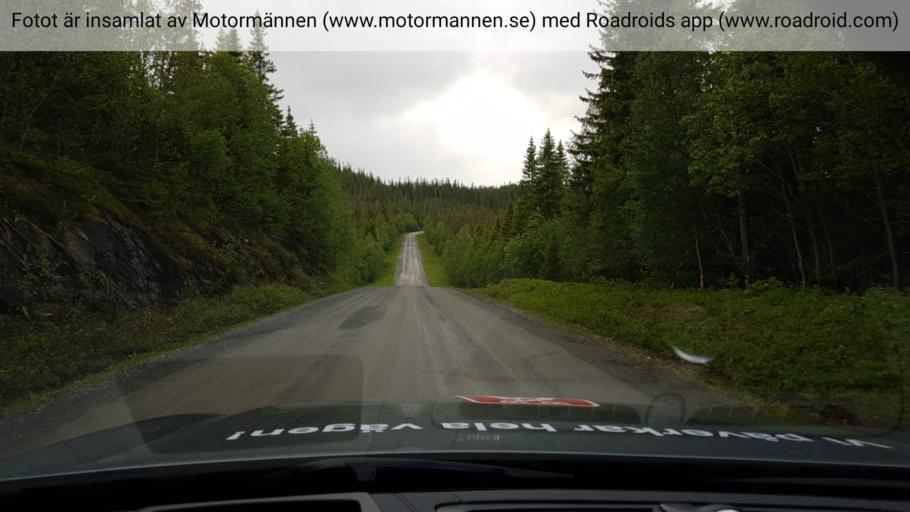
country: SE
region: Jaemtland
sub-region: Are Kommun
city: Are
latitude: 63.7154
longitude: 12.6202
